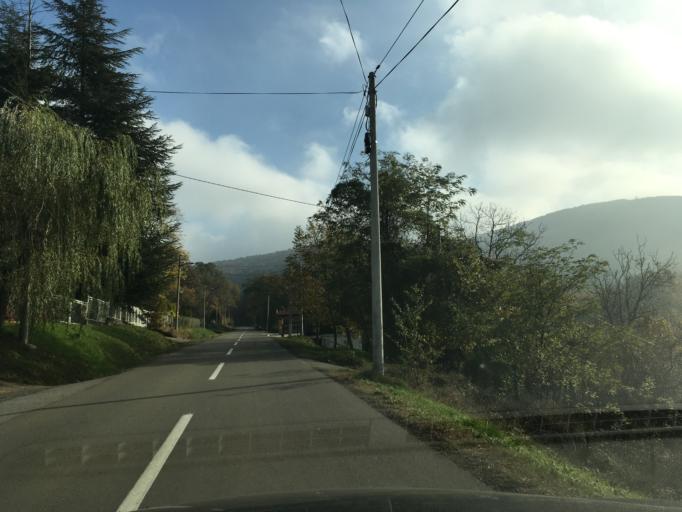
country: RS
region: Central Serbia
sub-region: Belgrade
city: Sopot
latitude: 44.4780
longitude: 20.5636
